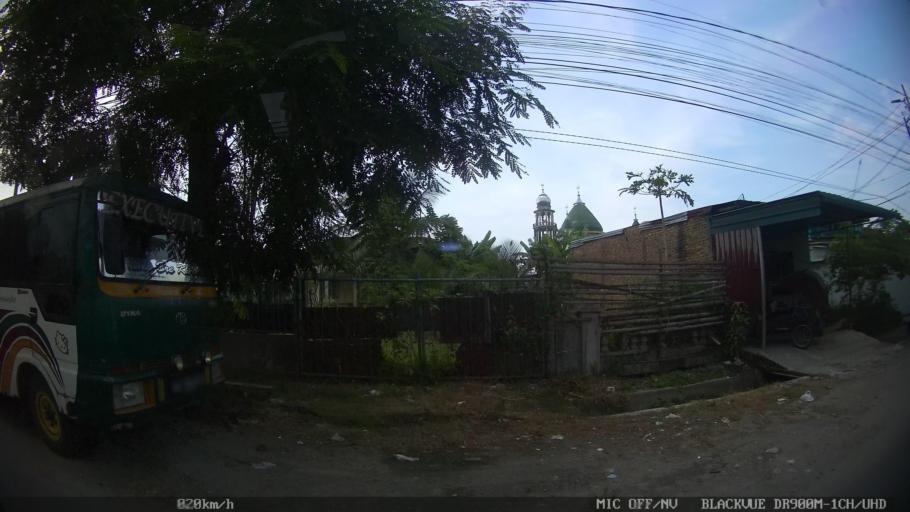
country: ID
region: North Sumatra
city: Medan
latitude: 3.6099
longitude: 98.6873
